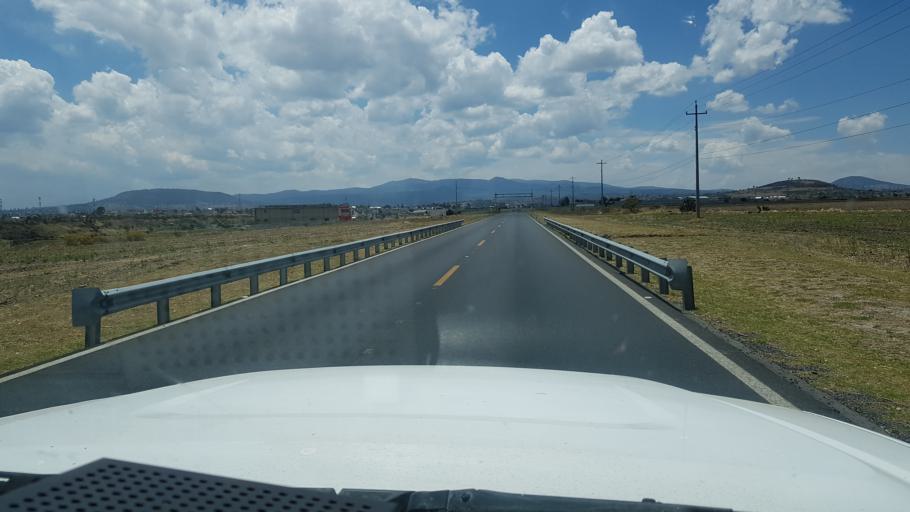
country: MX
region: Hidalgo
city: Calpulalpan
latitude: 19.6076
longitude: -98.5614
